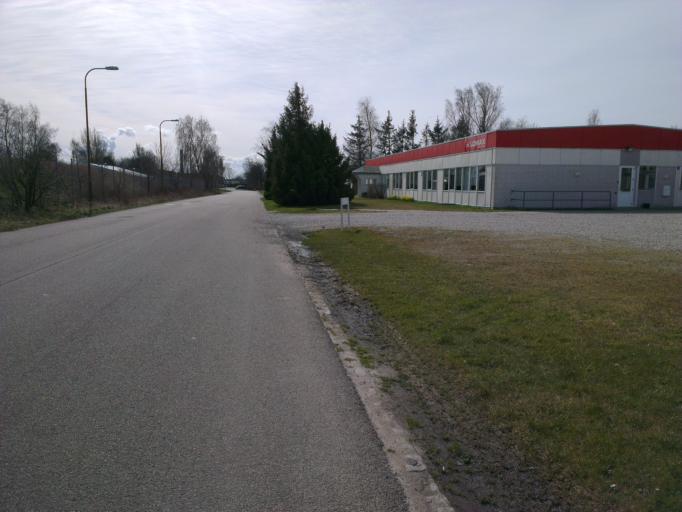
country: DK
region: Capital Region
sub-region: Frederikssund Kommune
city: Frederikssund
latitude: 55.8495
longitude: 12.0673
